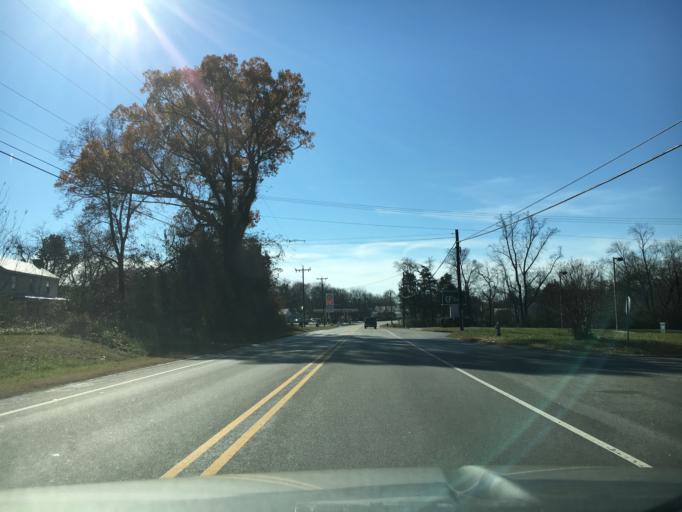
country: US
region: Virginia
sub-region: Cumberland County
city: Cumberland
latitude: 37.5015
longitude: -78.2406
